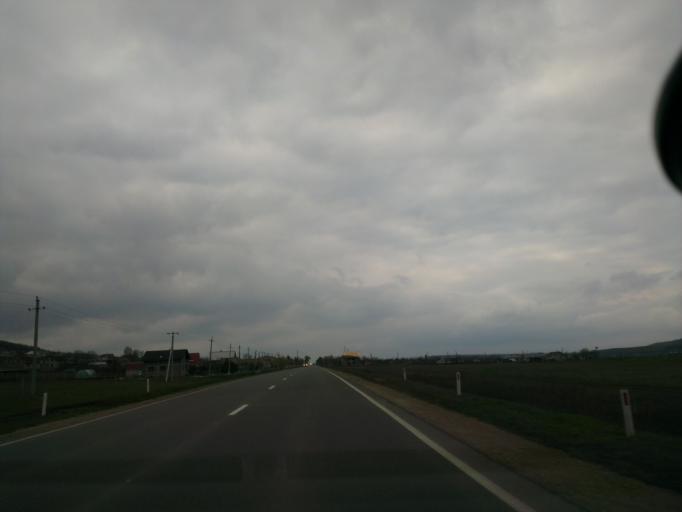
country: MD
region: Cimislia
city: Cimislia
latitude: 46.5732
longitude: 28.7534
